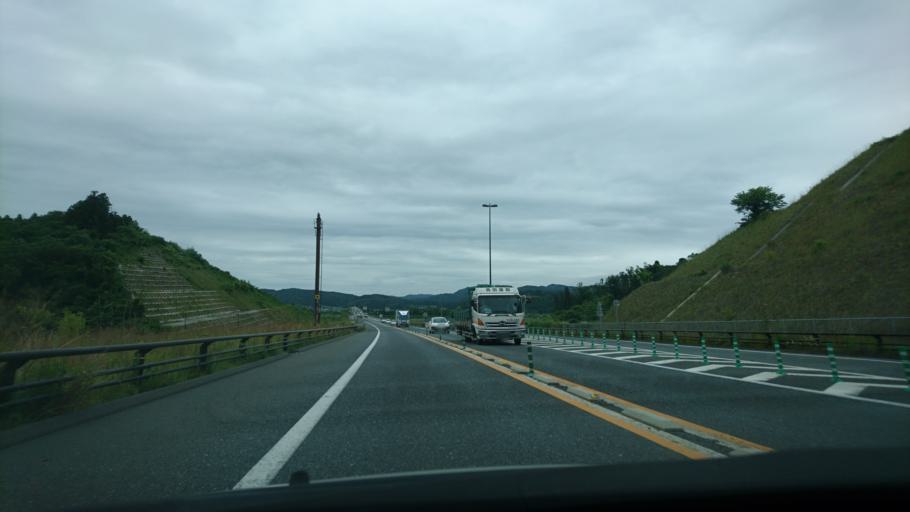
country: JP
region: Miyagi
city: Wakuya
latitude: 38.5965
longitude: 141.2820
